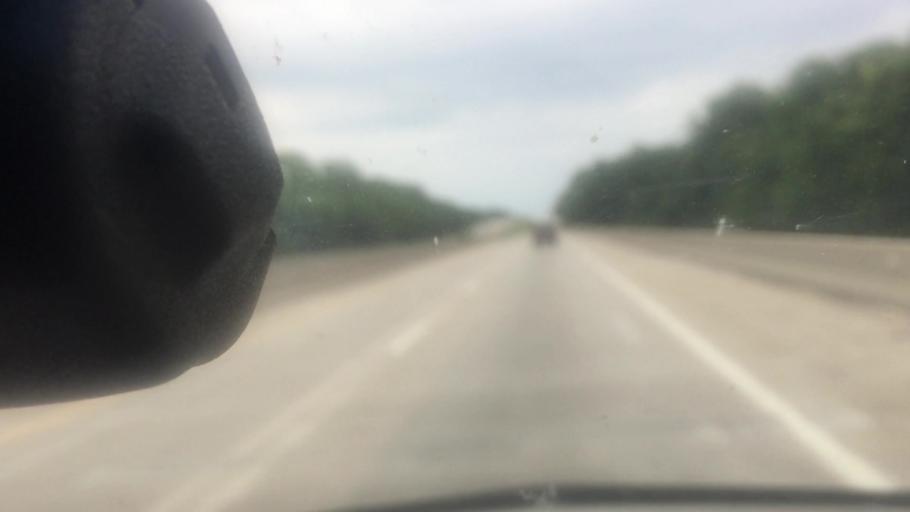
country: US
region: Illinois
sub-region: Sangamon County
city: Sherman
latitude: 39.8713
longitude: -89.5965
